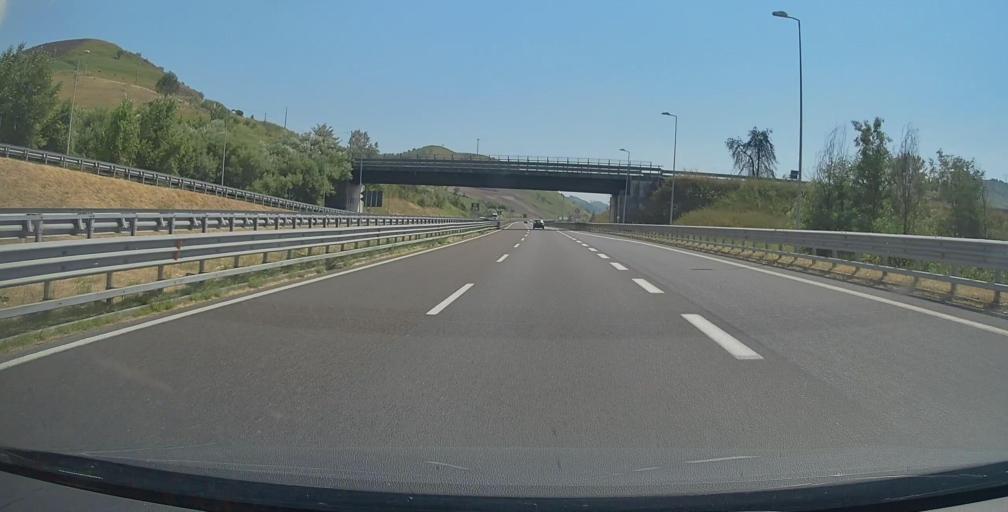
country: IT
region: Calabria
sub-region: Provincia di Vibo-Valentia
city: San Gregorio d'Ippona
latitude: 38.6244
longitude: 16.1606
